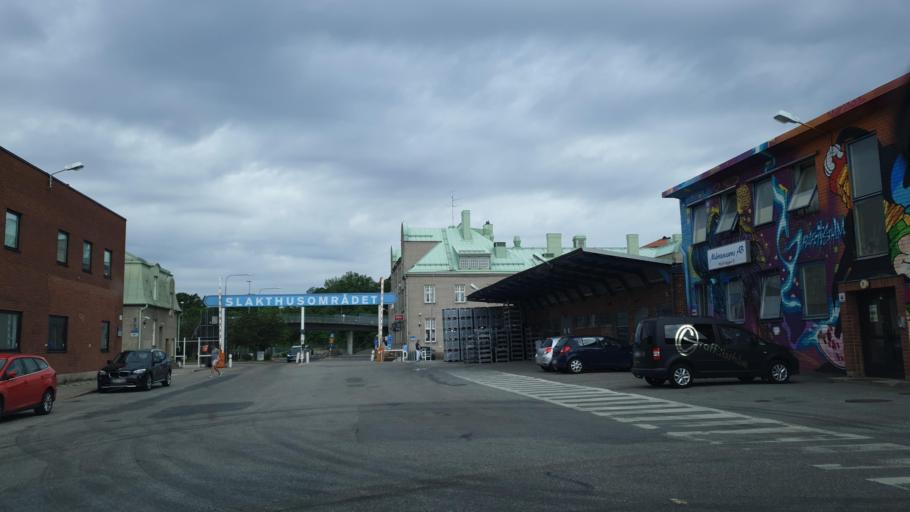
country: SE
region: Stockholm
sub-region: Stockholms Kommun
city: Arsta
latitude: 59.2925
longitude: 18.0762
